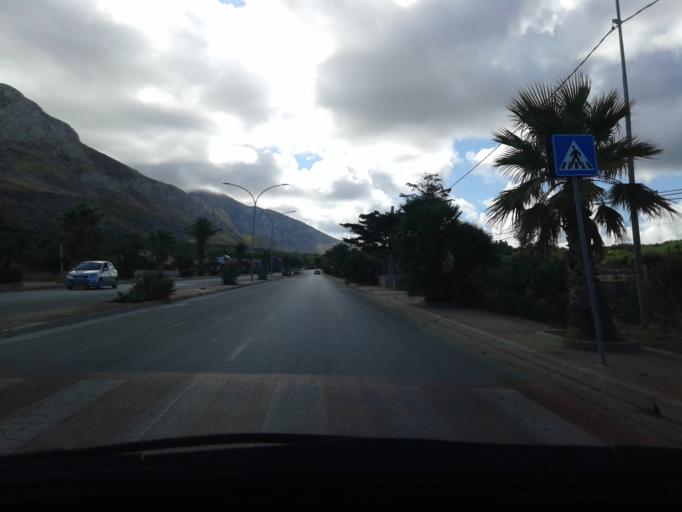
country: IT
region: Sicily
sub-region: Trapani
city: San Vito Lo Capo
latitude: 38.1623
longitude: 12.7365
